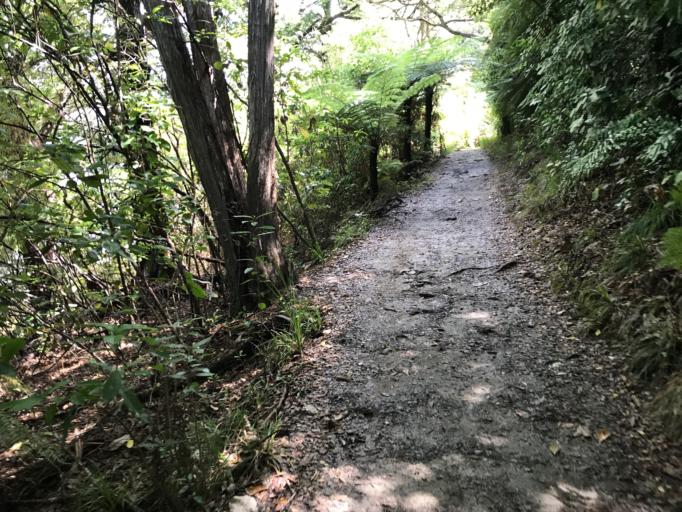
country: NZ
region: Marlborough
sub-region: Marlborough District
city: Picton
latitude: -41.2599
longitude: 173.9325
